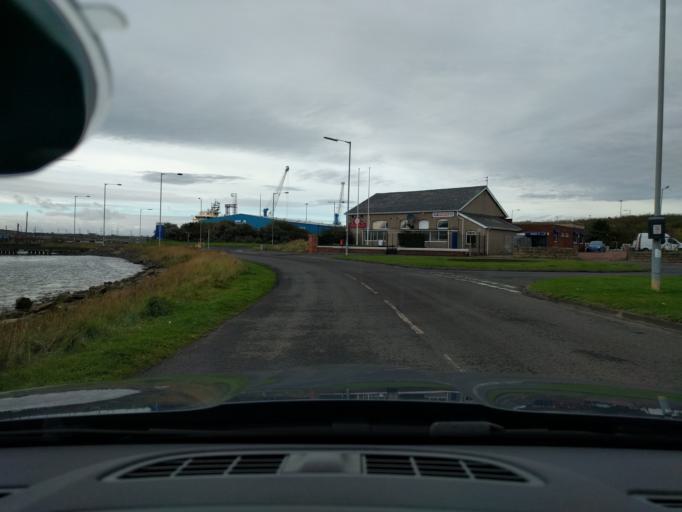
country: GB
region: England
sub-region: Northumberland
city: Blyth
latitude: 55.1351
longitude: -1.5110
